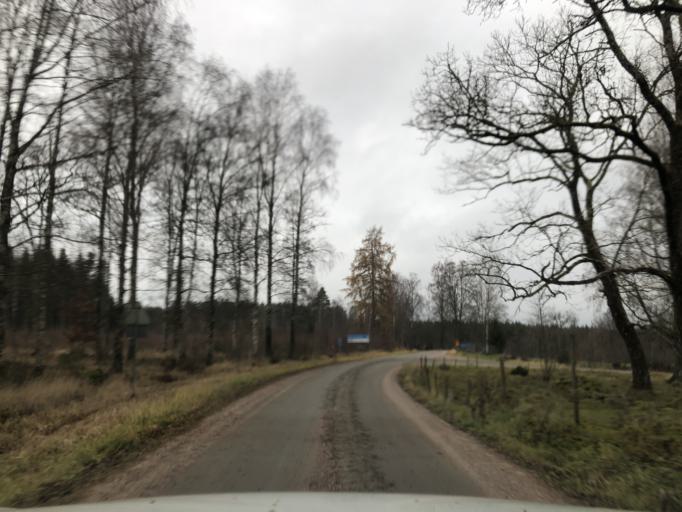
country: SE
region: Vaestra Goetaland
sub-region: Ulricehamns Kommun
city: Ulricehamn
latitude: 57.8521
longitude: 13.6337
